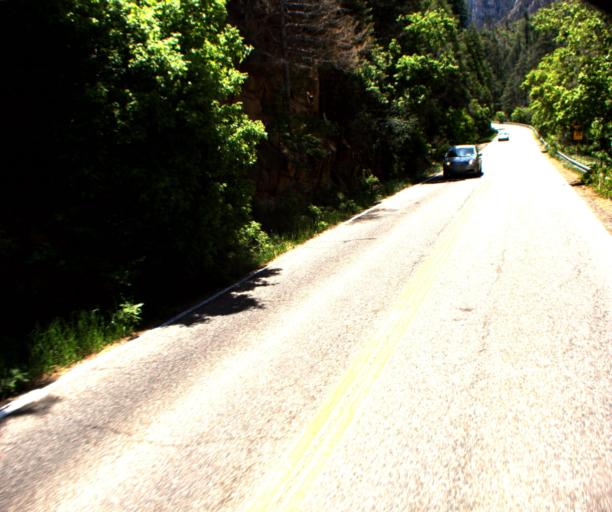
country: US
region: Arizona
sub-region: Coconino County
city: Sedona
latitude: 34.9723
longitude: -111.7486
